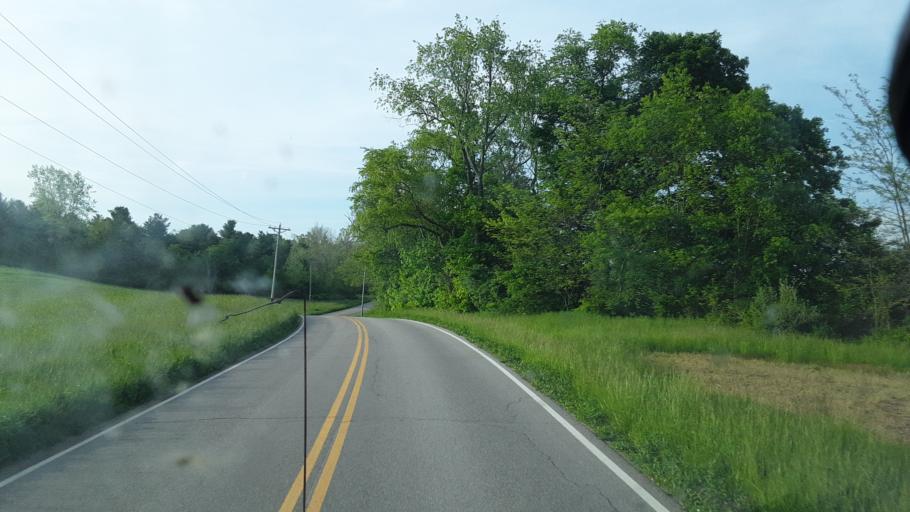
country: US
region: Ohio
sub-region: Ross County
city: Kingston
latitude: 39.5083
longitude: -82.6992
